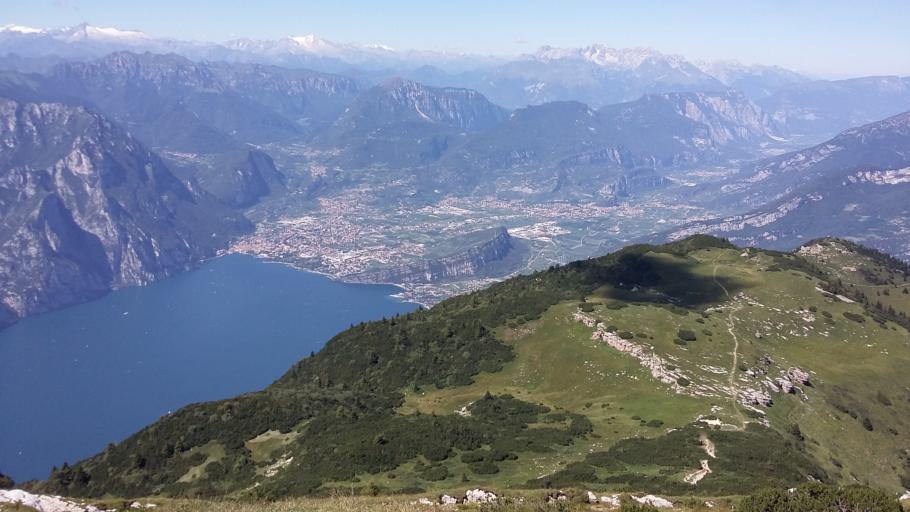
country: IT
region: Trentino-Alto Adige
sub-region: Provincia di Trento
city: Torbole sul Garda
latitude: 45.8123
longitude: 10.8902
